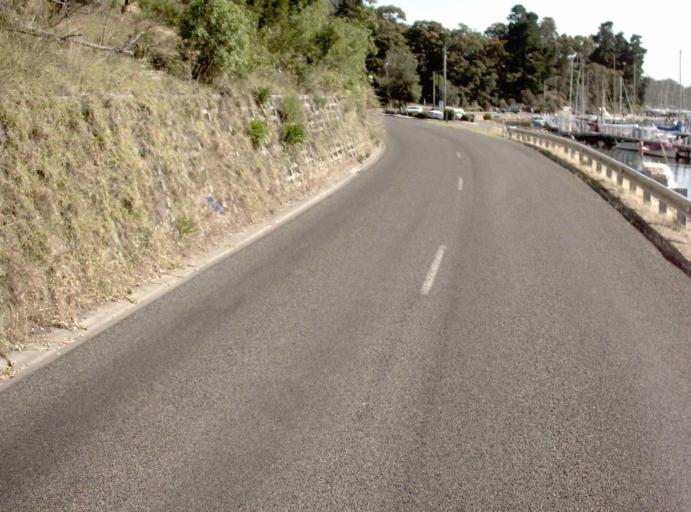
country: AU
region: Victoria
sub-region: East Gippsland
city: Lakes Entrance
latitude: -37.8888
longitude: 147.8566
